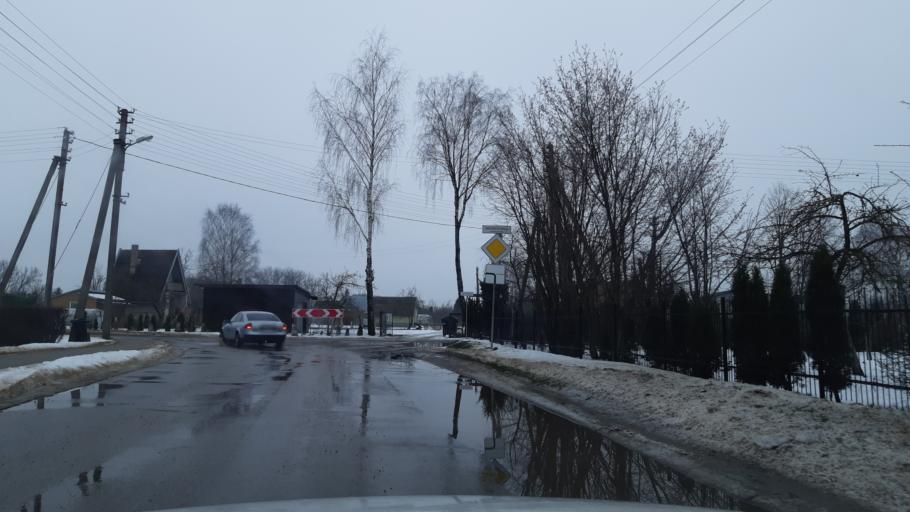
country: LT
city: Vilkaviskis
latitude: 54.6451
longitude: 23.0184
